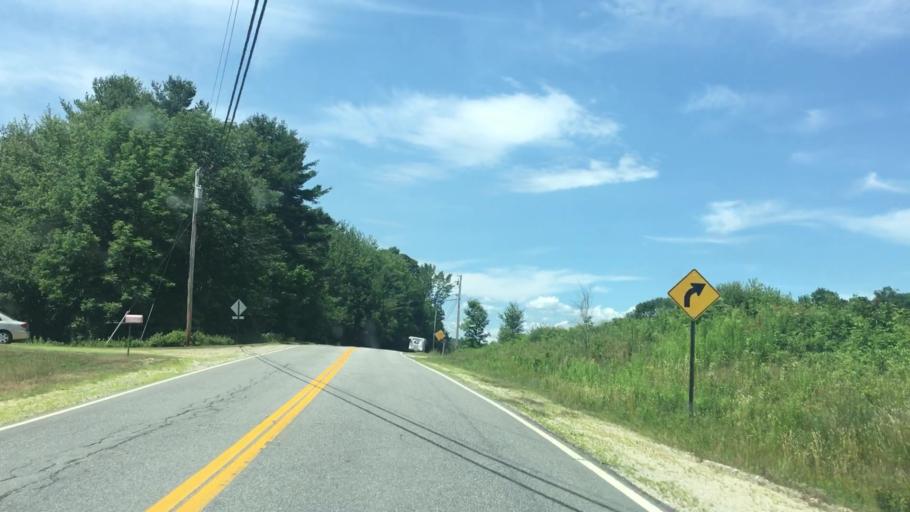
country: US
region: Maine
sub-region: Androscoggin County
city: Livermore
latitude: 44.3842
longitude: -70.2094
